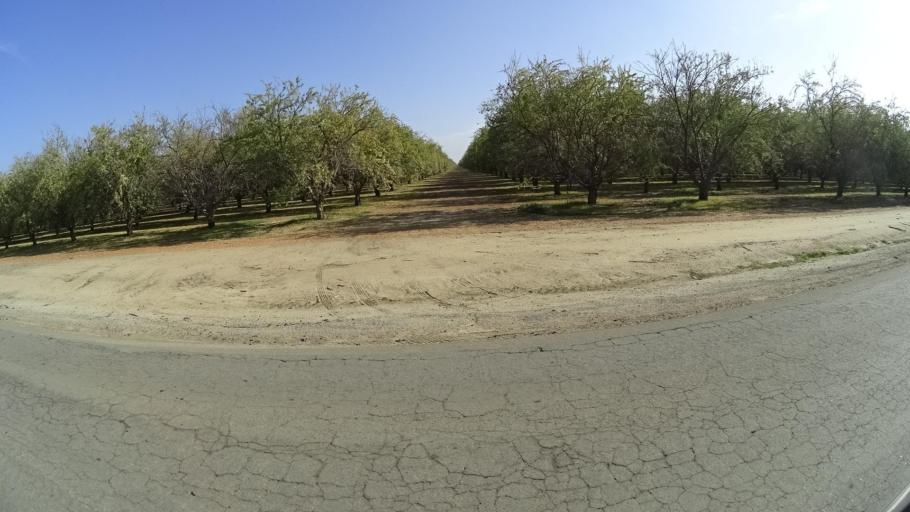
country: US
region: California
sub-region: Kern County
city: McFarland
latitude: 35.6439
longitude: -119.1690
